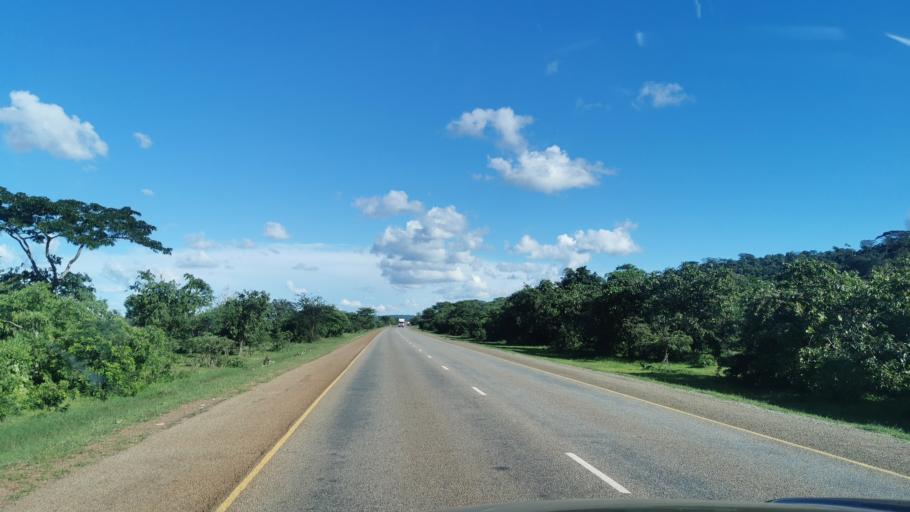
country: TZ
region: Geita
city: Masumbwe
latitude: -3.7175
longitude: 32.2914
